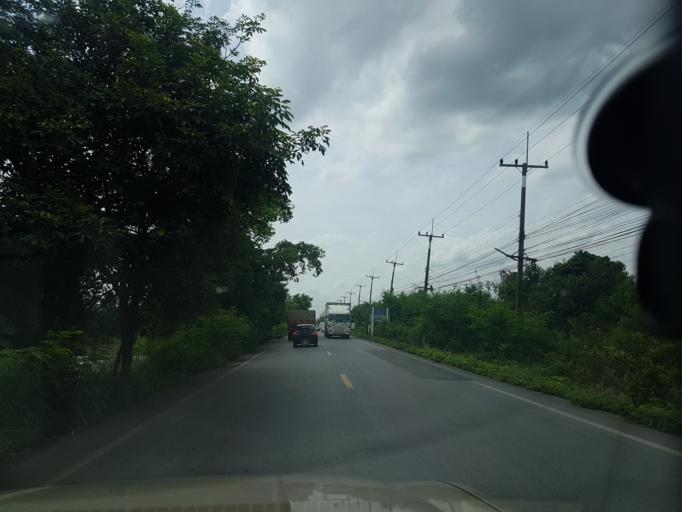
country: TH
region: Sara Buri
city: Nong Khae
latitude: 14.3075
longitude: 100.8875
